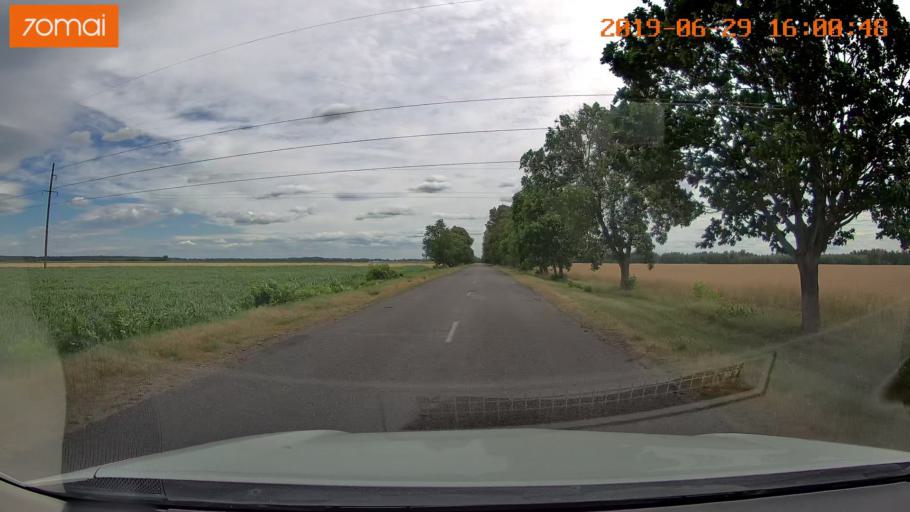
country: BY
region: Brest
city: Luninyets
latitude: 52.2556
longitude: 27.0171
